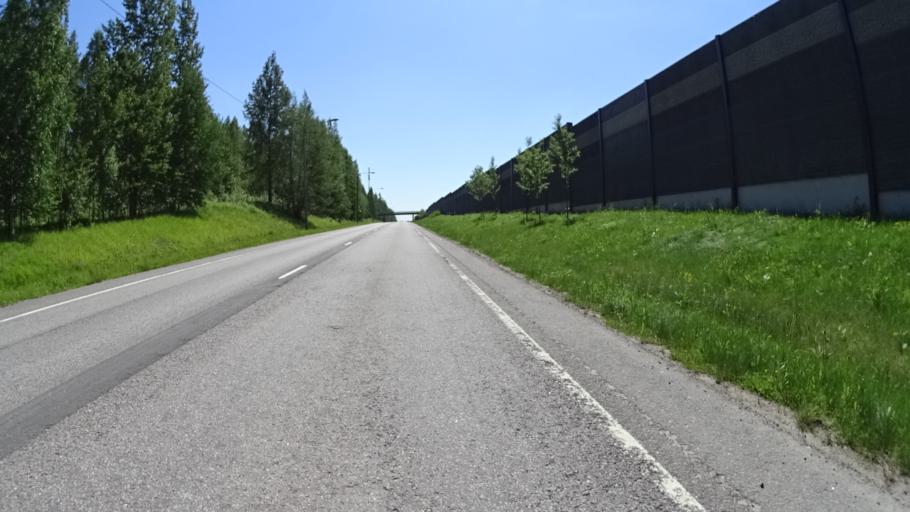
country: FI
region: Uusimaa
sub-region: Helsinki
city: Kilo
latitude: 60.3244
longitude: 24.8288
